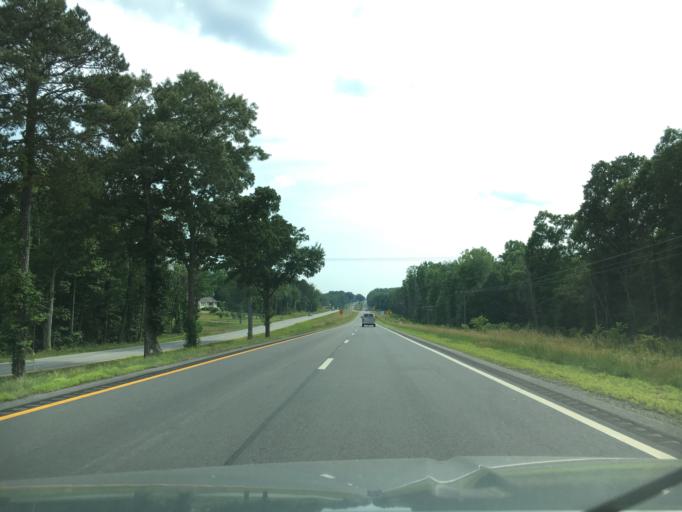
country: US
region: Virginia
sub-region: Mecklenburg County
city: Chase City
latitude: 36.9085
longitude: -78.5302
